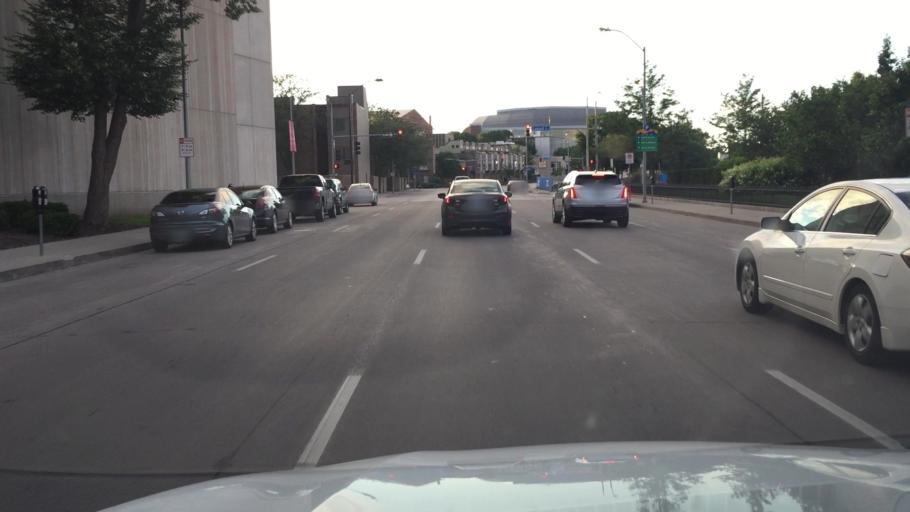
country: US
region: Iowa
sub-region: Polk County
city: Des Moines
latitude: 41.5873
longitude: -93.6199
